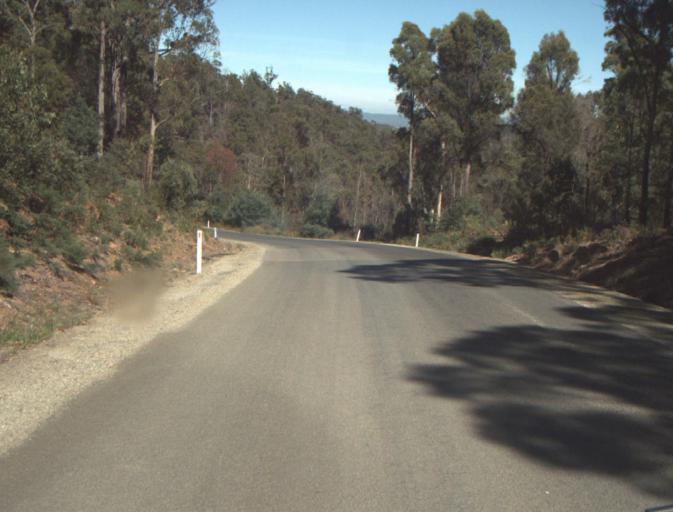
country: AU
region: Tasmania
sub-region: Launceston
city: Mayfield
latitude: -41.3357
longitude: 147.1992
